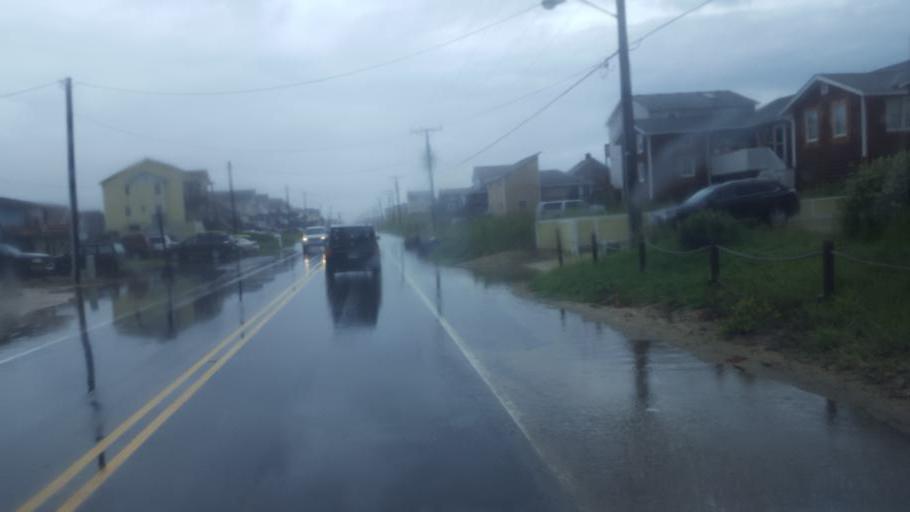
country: US
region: North Carolina
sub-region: Dare County
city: Kill Devil Hills
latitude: 36.0394
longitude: -75.6725
